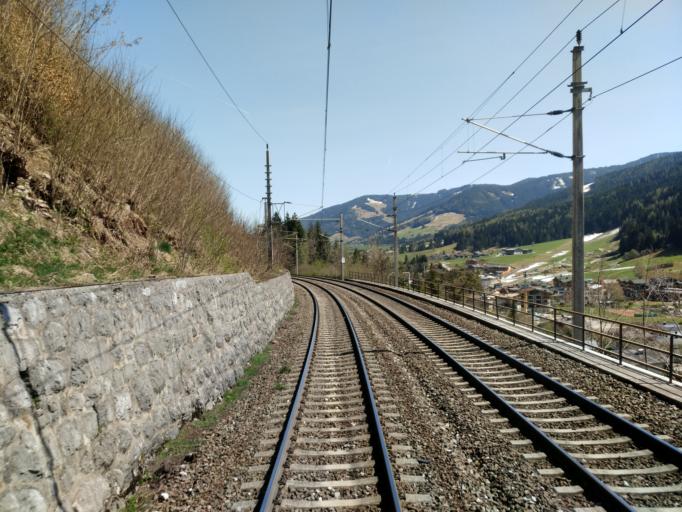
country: AT
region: Salzburg
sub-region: Politischer Bezirk Zell am See
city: Leogang
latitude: 47.4429
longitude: 12.7106
